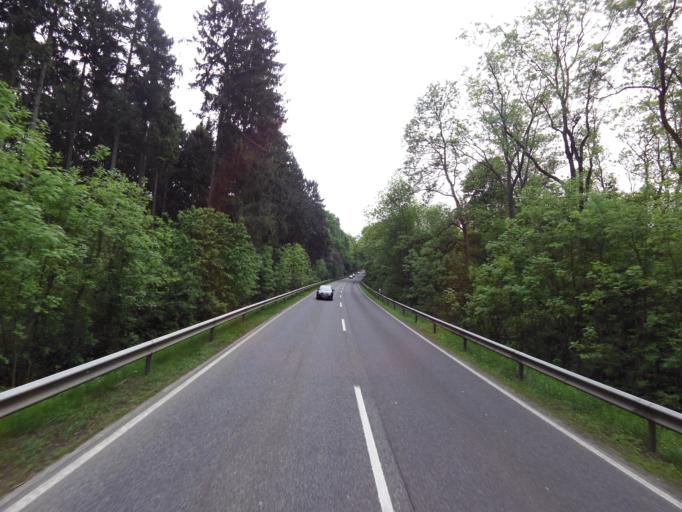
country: DE
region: Rheinland-Pfalz
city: Waldesch
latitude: 50.3094
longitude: 7.5541
